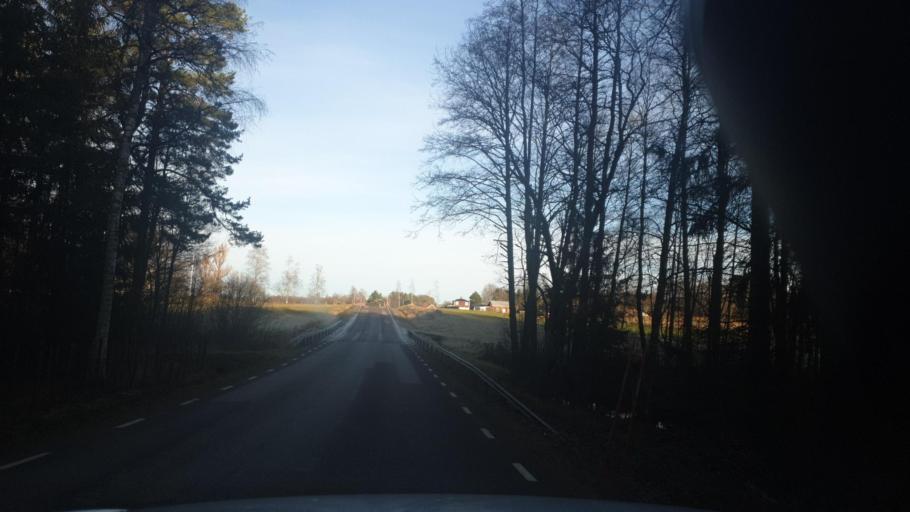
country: SE
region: Vaermland
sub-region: Grums Kommun
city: Slottsbron
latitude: 59.4702
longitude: 12.8792
